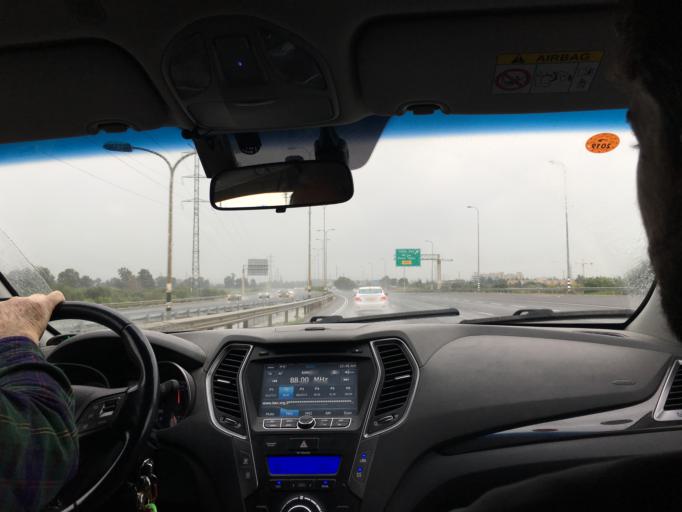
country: IL
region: Tel Aviv
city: Ramat HaSharon
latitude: 32.1216
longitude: 34.8624
